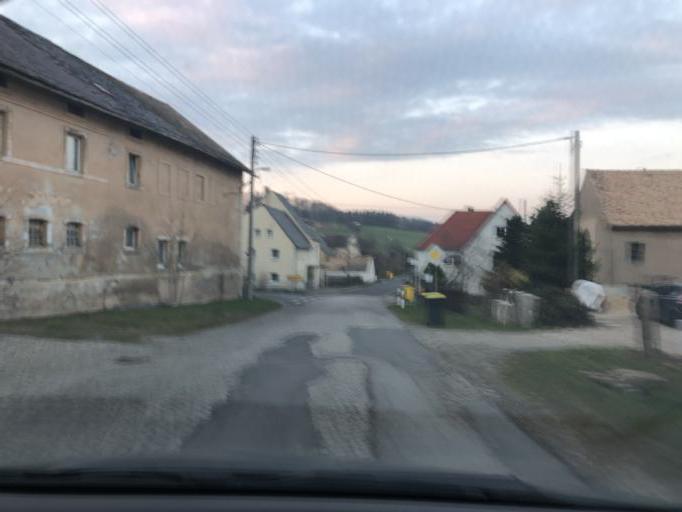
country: DE
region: Saxony
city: Kamenz
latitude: 51.2395
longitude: 14.0831
